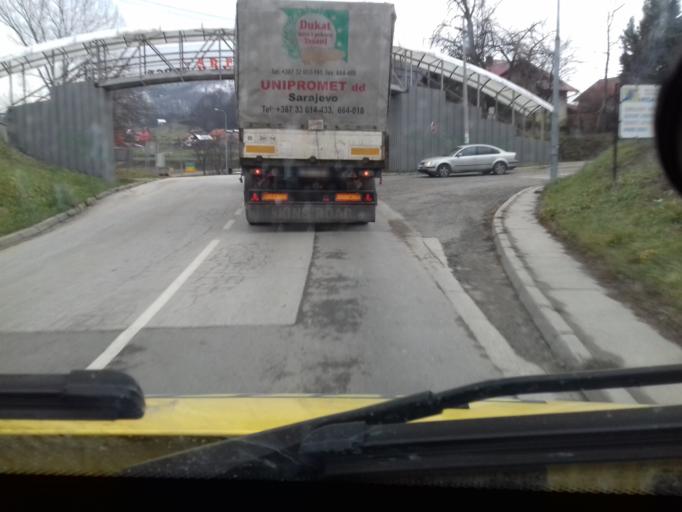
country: BA
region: Federation of Bosnia and Herzegovina
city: Zepce
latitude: 44.4314
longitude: 18.0390
